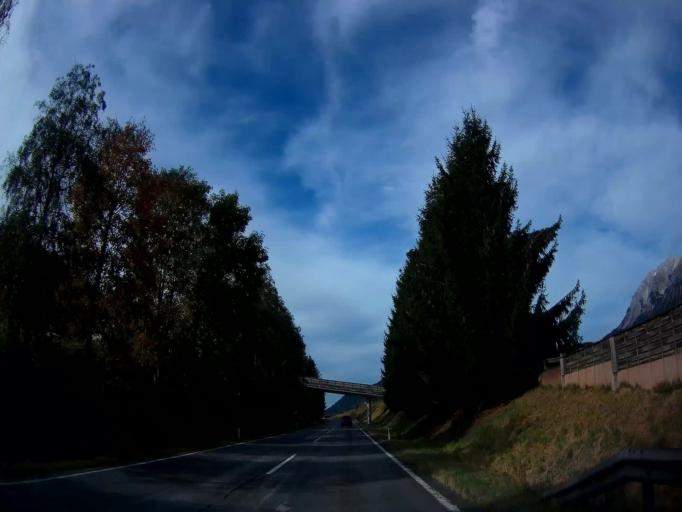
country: AT
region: Styria
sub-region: Politischer Bezirk Liezen
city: Haus
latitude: 47.4030
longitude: 13.7279
